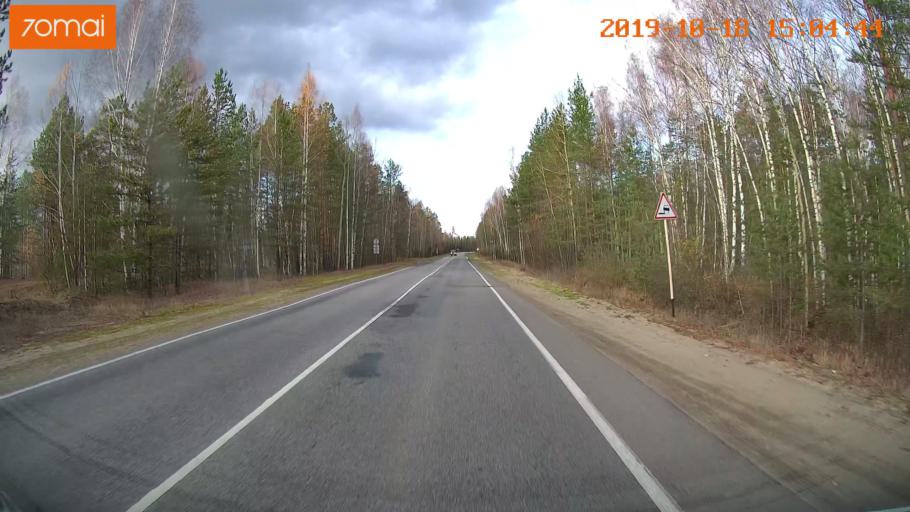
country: RU
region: Vladimir
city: Kurlovo
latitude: 55.5056
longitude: 40.5712
